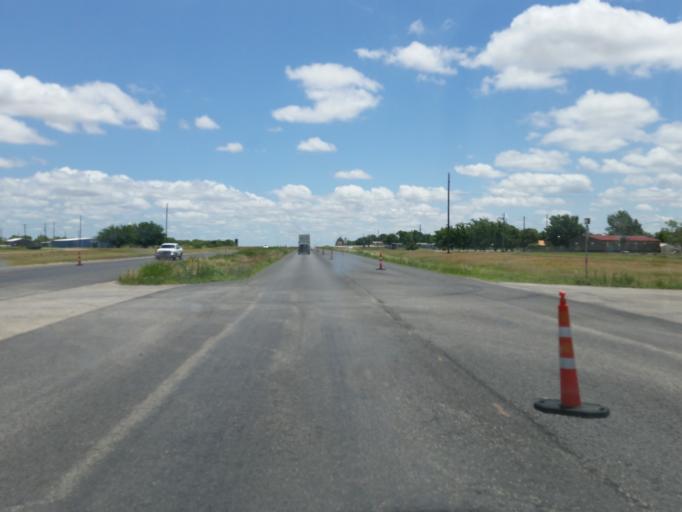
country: US
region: Texas
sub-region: Scurry County
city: Snyder
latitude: 32.7271
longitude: -100.8947
